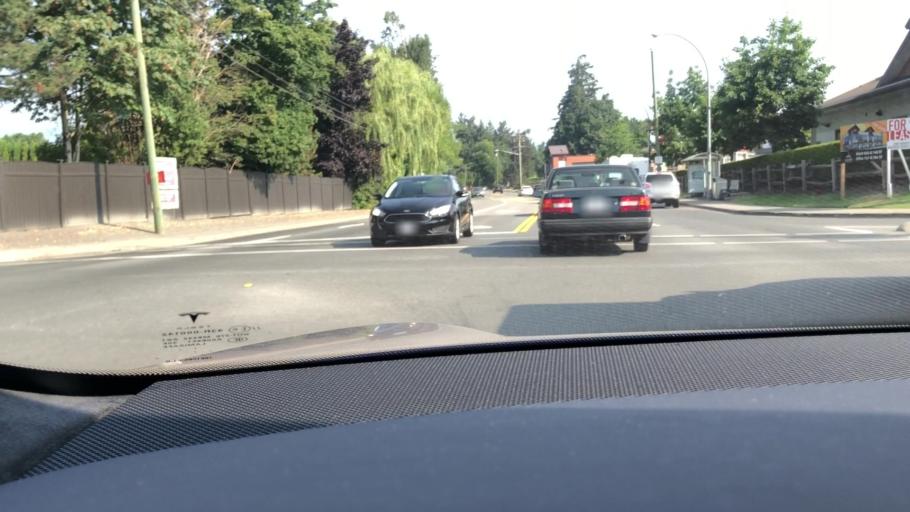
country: CA
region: British Columbia
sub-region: Fraser Valley Regional District
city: Chilliwack
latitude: 49.1228
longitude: -121.9598
